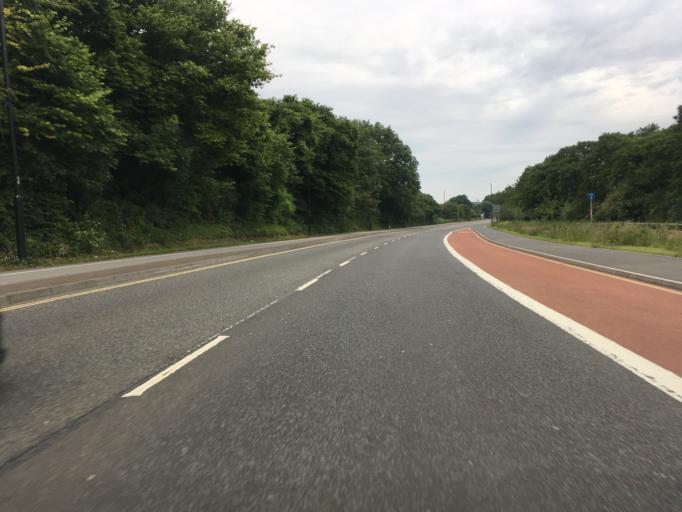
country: GB
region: England
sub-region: Bristol
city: Bristol
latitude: 51.4222
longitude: -2.6043
